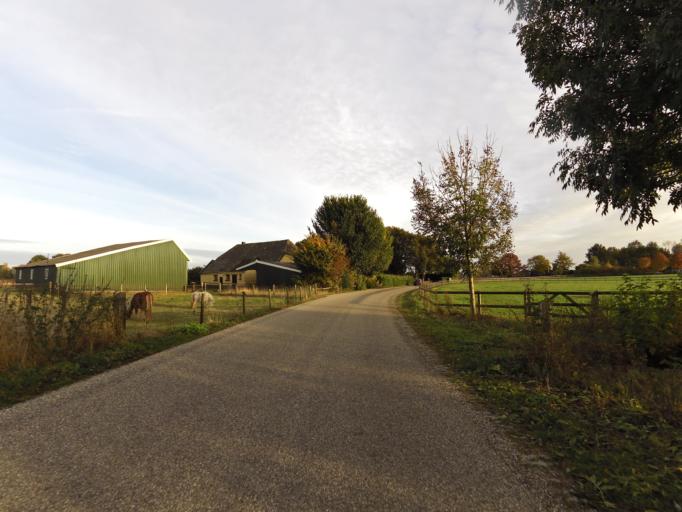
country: NL
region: Gelderland
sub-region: Gemeente Doesburg
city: Doesburg
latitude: 51.9731
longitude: 6.1773
